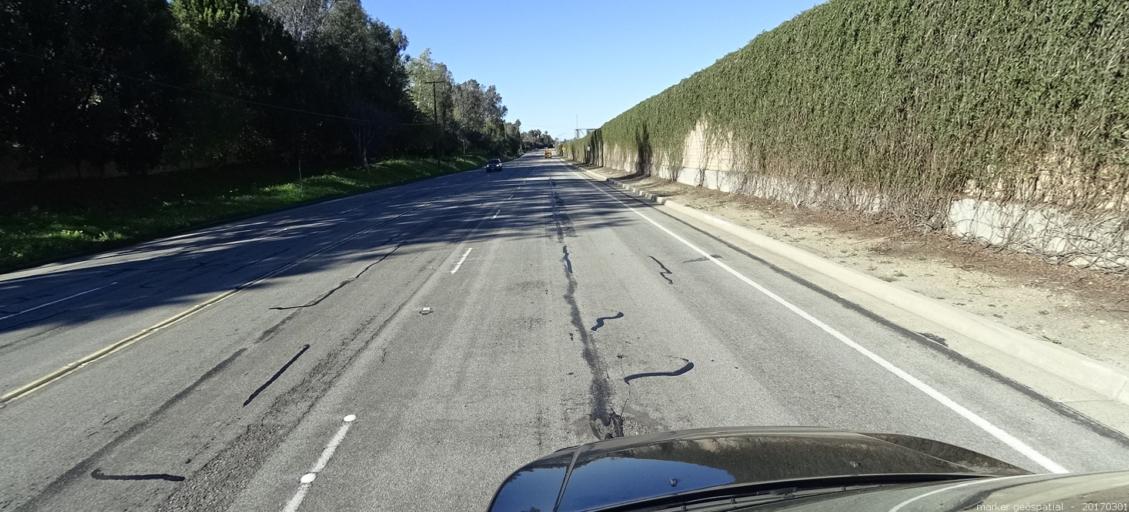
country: US
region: California
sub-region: Orange County
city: Villa Park
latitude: 33.8464
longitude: -117.8196
